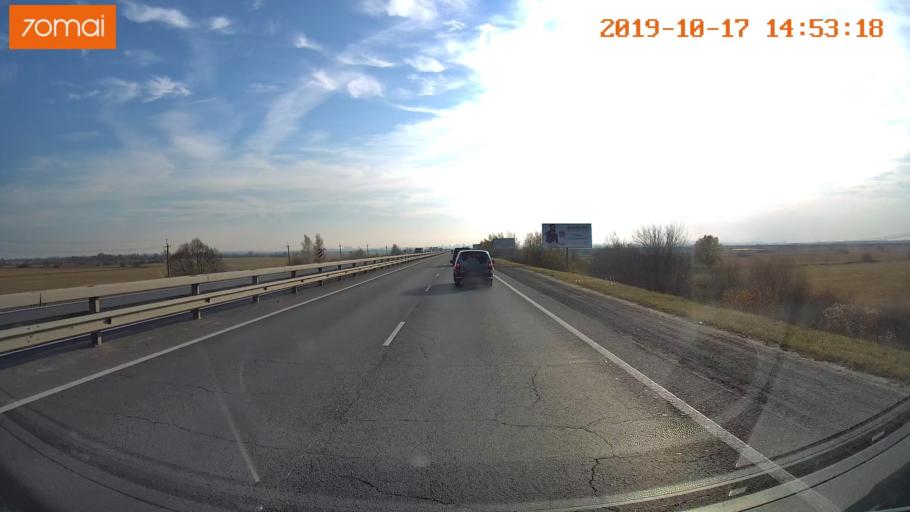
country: RU
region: Rjazan
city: Polyany
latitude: 54.6959
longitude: 39.8391
